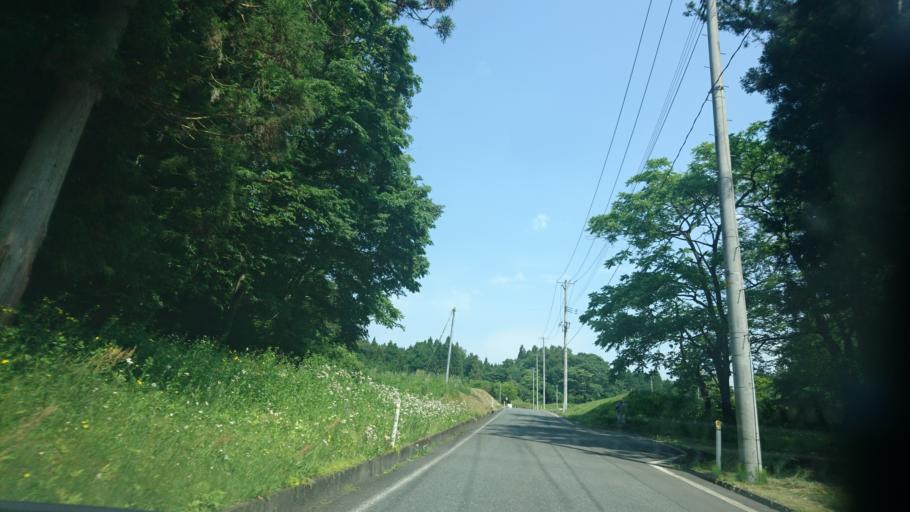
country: JP
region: Iwate
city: Ichinoseki
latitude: 38.9099
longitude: 141.3174
